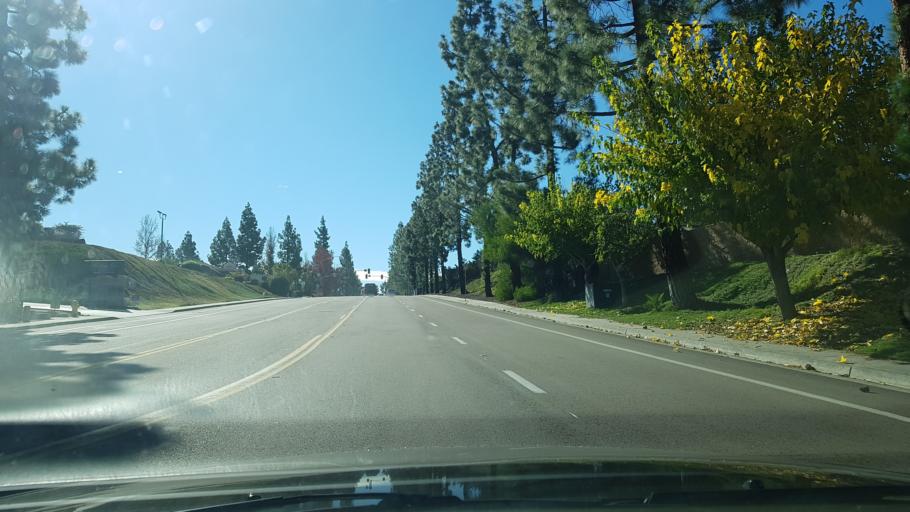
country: US
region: California
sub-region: San Diego County
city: Escondido
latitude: 33.0353
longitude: -117.0797
